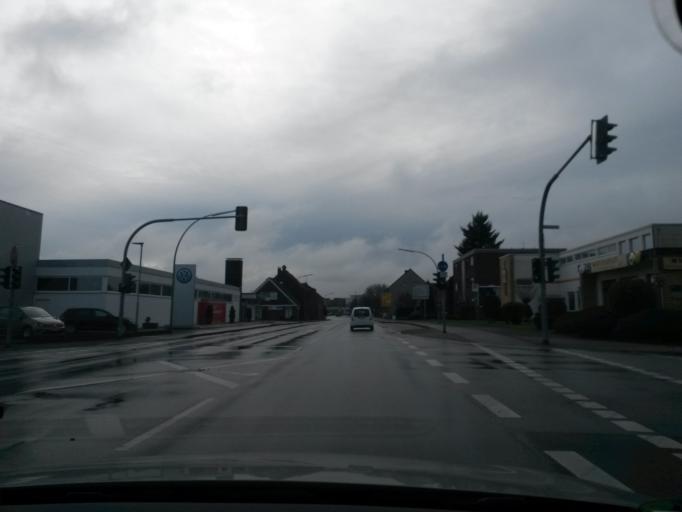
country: DE
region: North Rhine-Westphalia
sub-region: Regierungsbezirk Dusseldorf
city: Kamp-Lintfort
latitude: 51.5101
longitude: 6.5428
